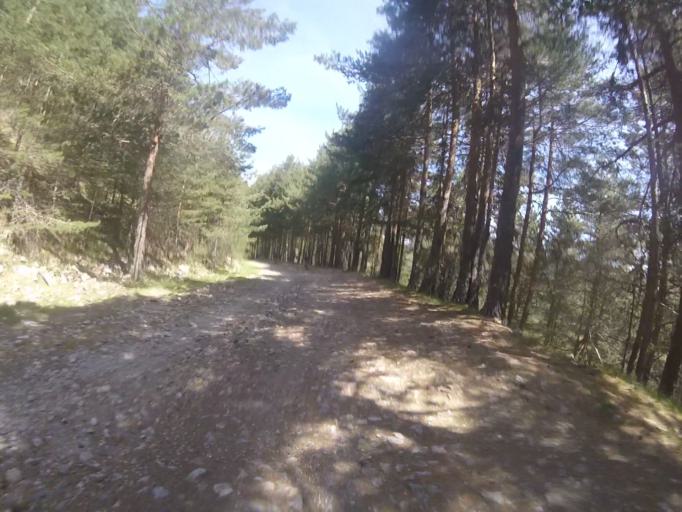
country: ES
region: Madrid
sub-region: Provincia de Madrid
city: Cercedilla
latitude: 40.8088
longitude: -4.0557
